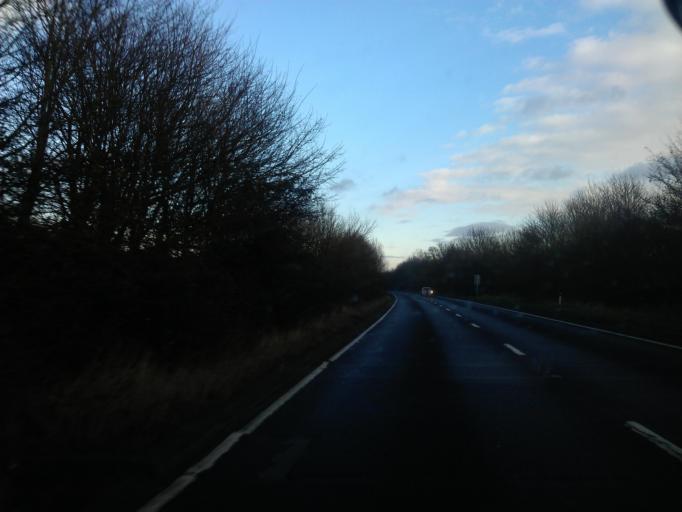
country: GB
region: England
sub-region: Essex
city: Mistley
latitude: 51.9085
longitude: 1.1186
